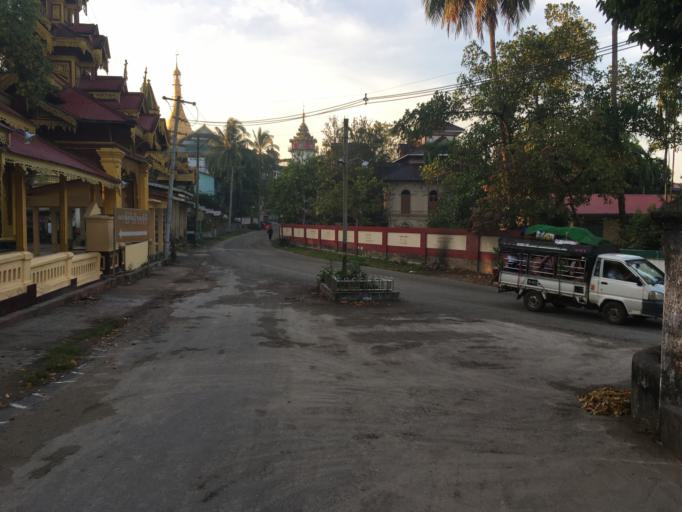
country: MM
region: Mon
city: Mawlamyine
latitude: 16.4915
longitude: 97.6280
